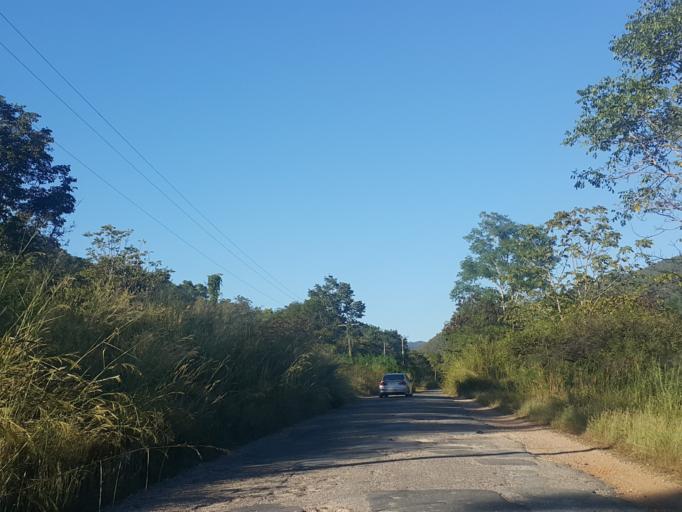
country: TH
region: Chiang Mai
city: San Sai
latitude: 18.9283
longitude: 99.1366
